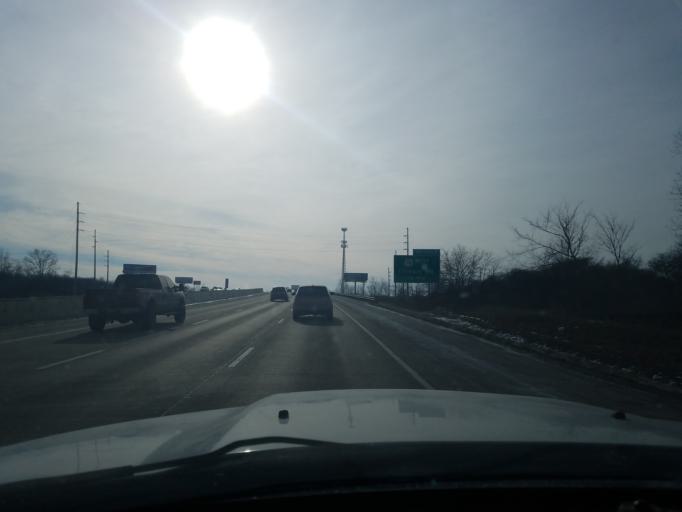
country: US
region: Indiana
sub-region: Allen County
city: Fort Wayne
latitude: 41.0877
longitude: -85.2227
